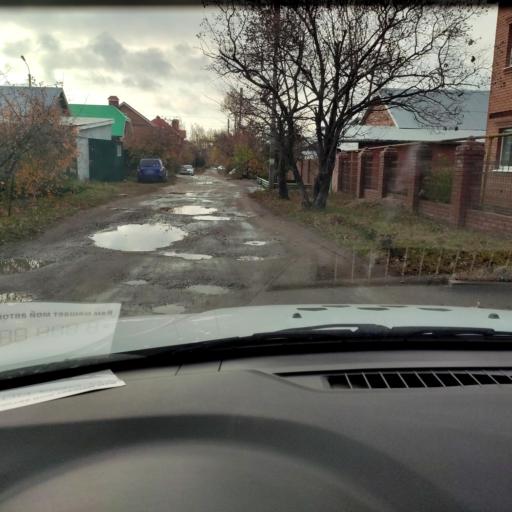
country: RU
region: Samara
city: Tol'yatti
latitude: 53.5350
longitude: 49.3983
